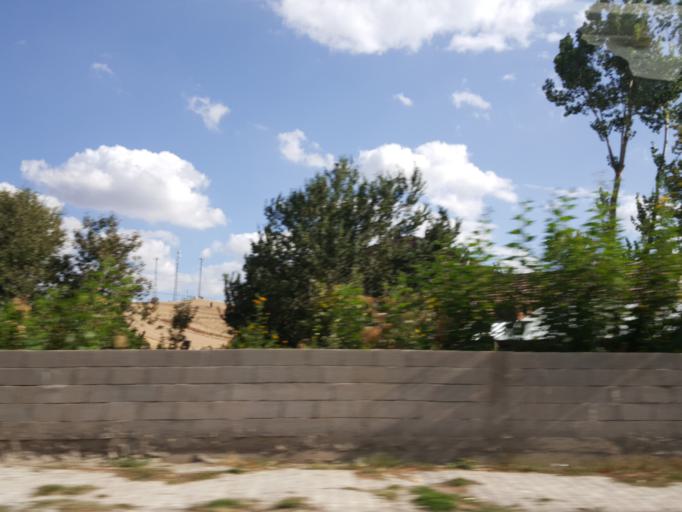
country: TR
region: Tokat
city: Sulusaray
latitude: 39.9889
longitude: 36.0802
